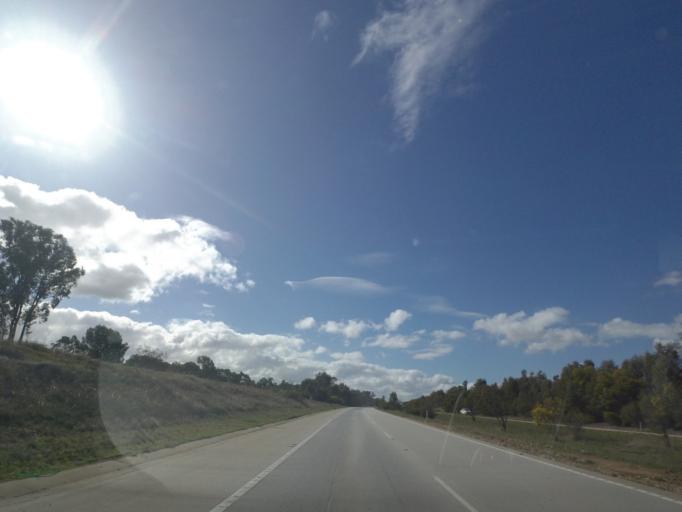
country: AU
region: New South Wales
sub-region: Albury Municipality
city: Lavington
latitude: -36.0280
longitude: 146.9778
